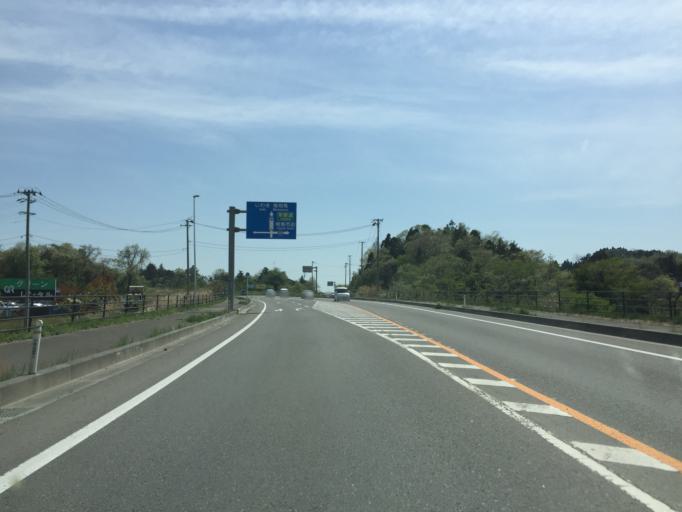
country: JP
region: Miyagi
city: Marumori
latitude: 37.8570
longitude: 140.9197
